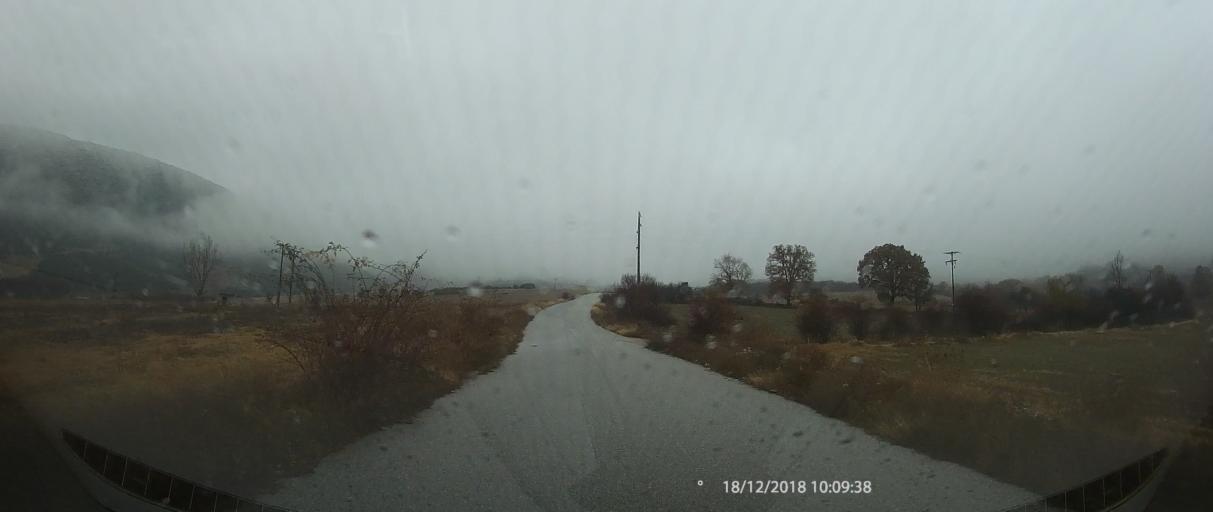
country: GR
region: Thessaly
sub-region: Nomos Larisis
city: Livadi
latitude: 40.0827
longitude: 22.2147
